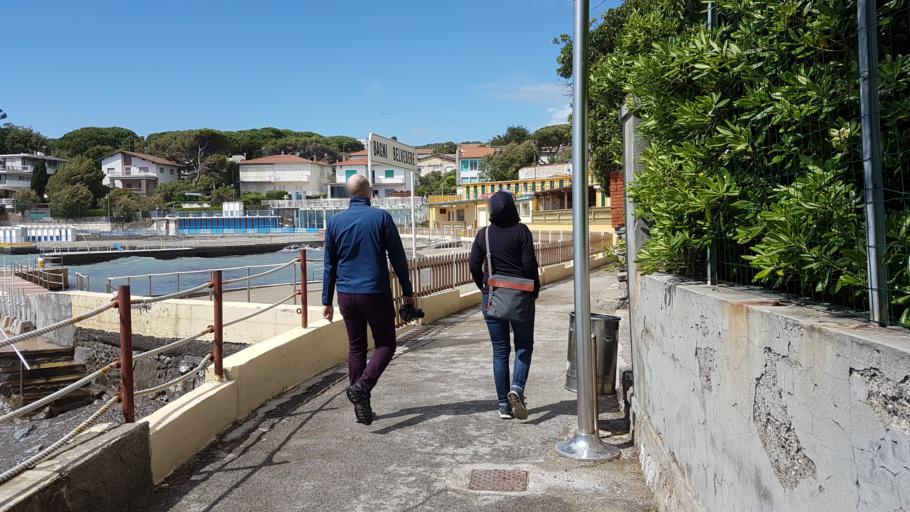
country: IT
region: Tuscany
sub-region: Provincia di Livorno
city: Rosignano Solvay-Castiglioncello
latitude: 43.4024
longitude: 10.4200
